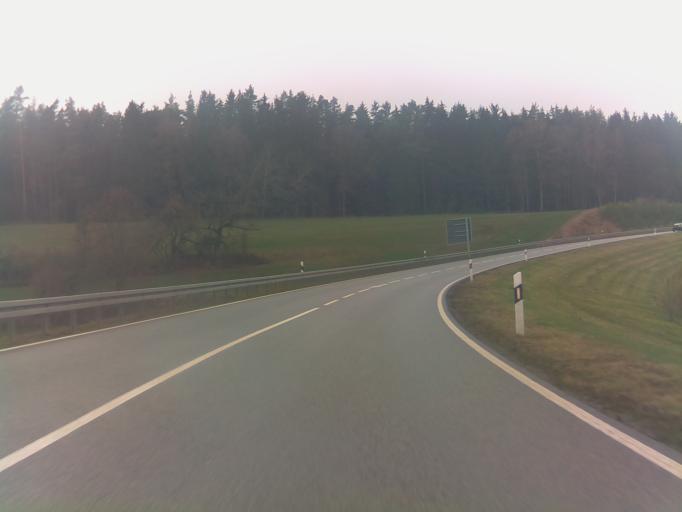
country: DE
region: Thuringia
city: Schleusingen
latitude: 50.4950
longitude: 10.7743
